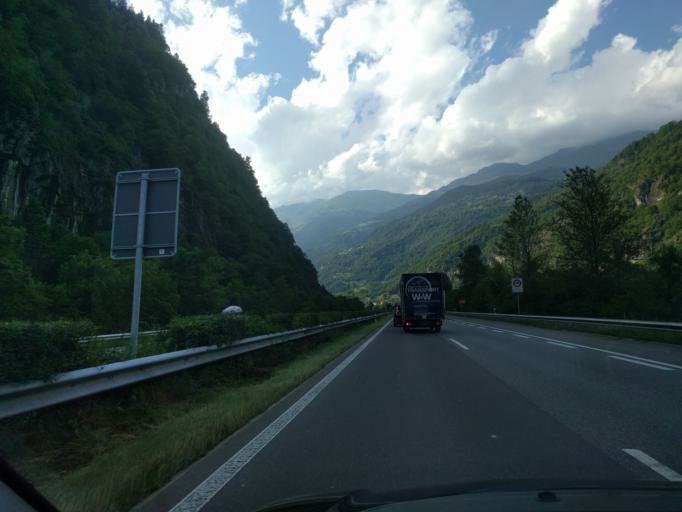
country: CH
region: Ticino
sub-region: Leventina District
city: Faido
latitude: 46.4581
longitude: 8.8254
